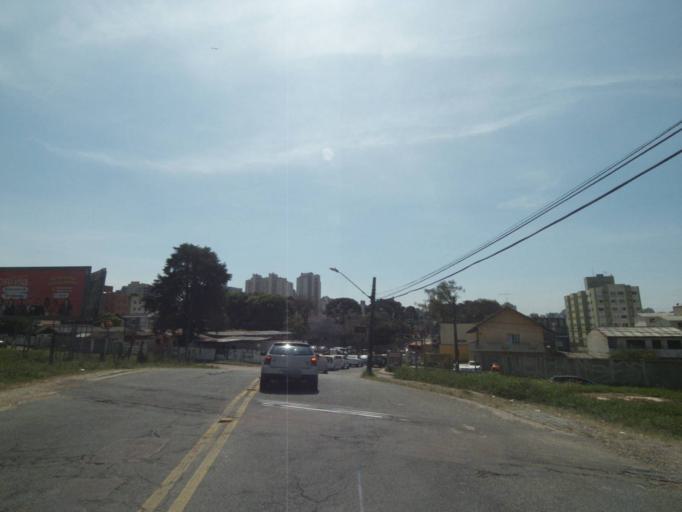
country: BR
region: Parana
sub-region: Curitiba
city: Curitiba
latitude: -25.4765
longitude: -49.2872
